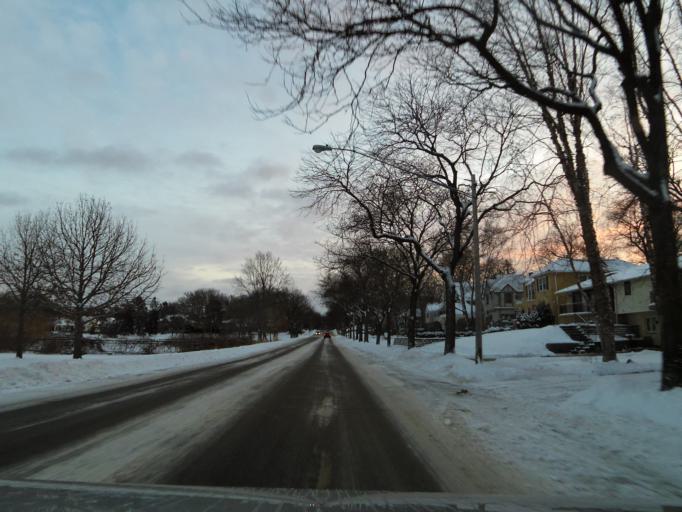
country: US
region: Minnesota
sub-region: Hennepin County
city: Saint Louis Park
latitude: 44.9362
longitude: -93.3214
